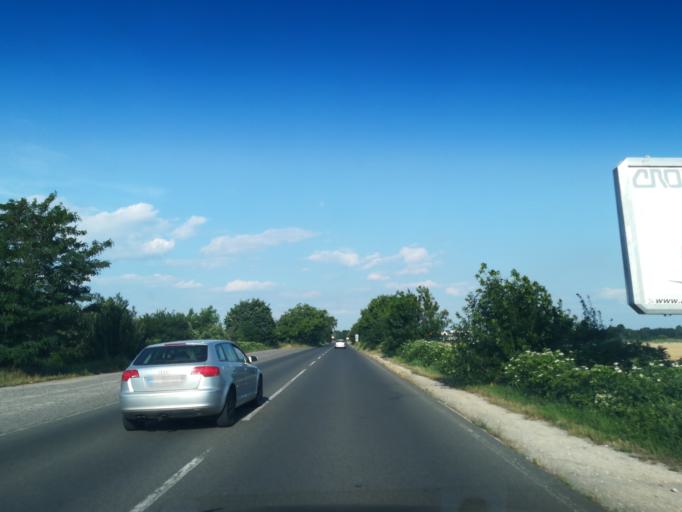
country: BG
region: Plovdiv
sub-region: Obshtina Plovdiv
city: Plovdiv
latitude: 42.1490
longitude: 24.8239
